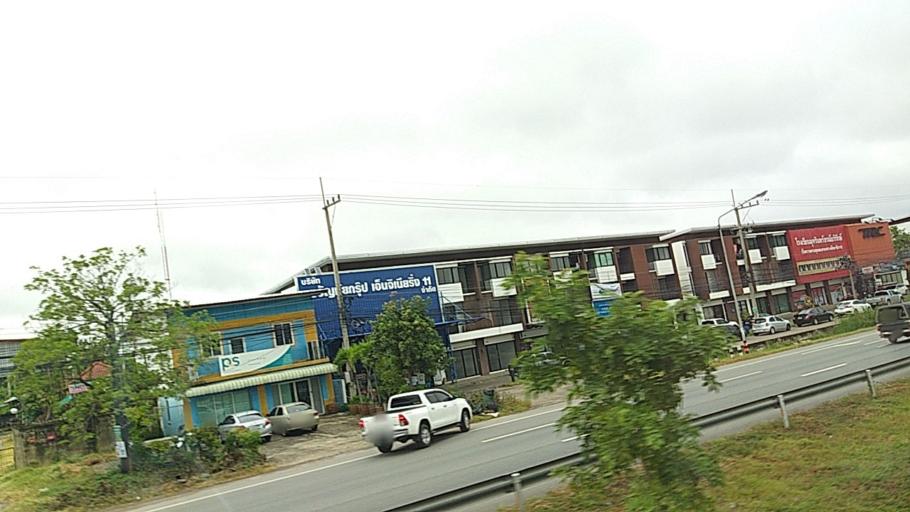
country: TH
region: Nakhon Ratchasima
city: Nakhon Ratchasima
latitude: 15.0328
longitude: 102.1424
